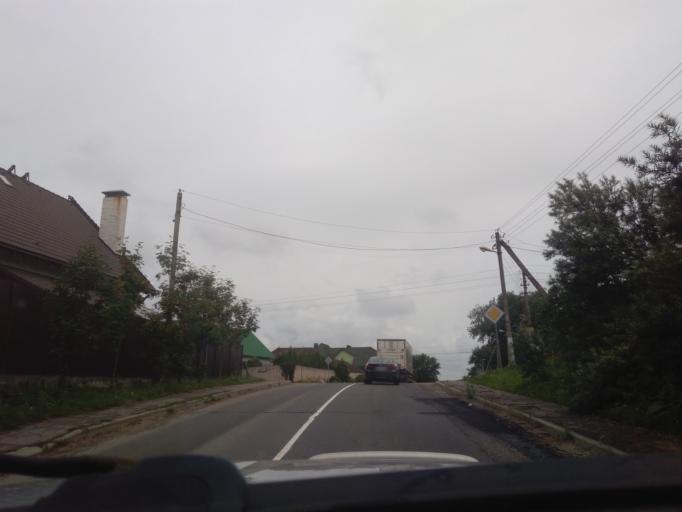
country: BY
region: Minsk
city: Zhdanovichy
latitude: 53.9171
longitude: 27.3900
